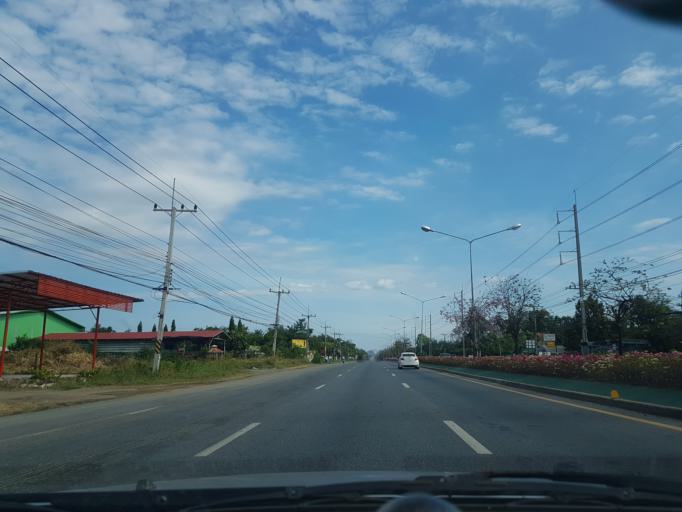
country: TH
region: Sara Buri
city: Phra Phutthabat
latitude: 14.7466
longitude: 100.7530
